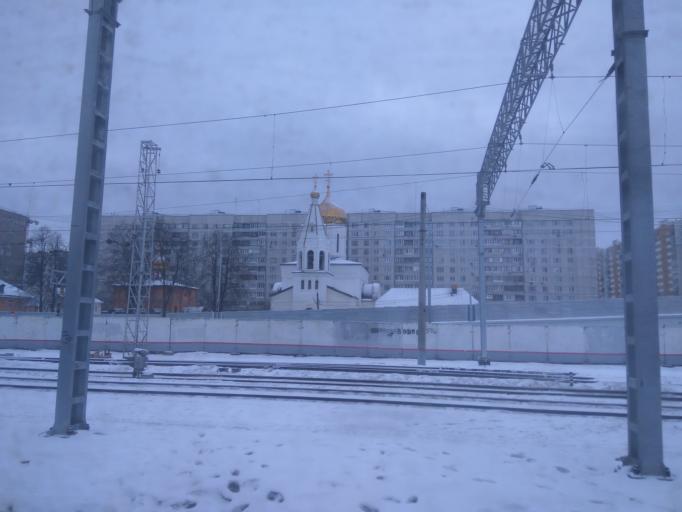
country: RU
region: Moskovskaya
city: Shcherbinka
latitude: 55.5094
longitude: 37.5620
